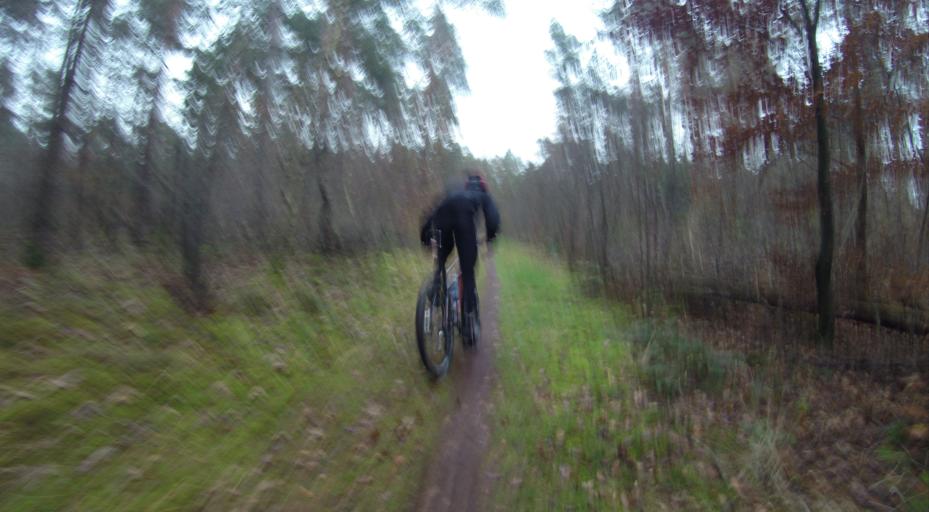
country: NL
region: Gelderland
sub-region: Gemeente Lochem
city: Almen
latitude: 52.1129
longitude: 6.3480
